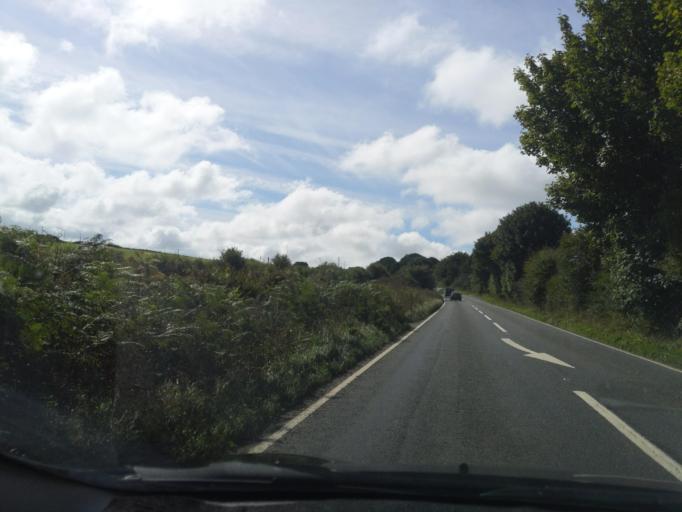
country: GB
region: England
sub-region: Cornwall
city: Camelford
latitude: 50.6547
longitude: -4.6211
